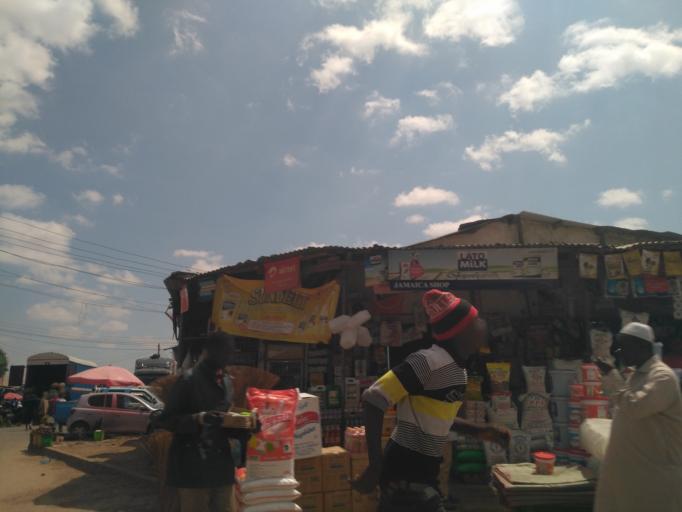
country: TZ
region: Dodoma
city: Dodoma
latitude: -6.1784
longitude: 35.7411
